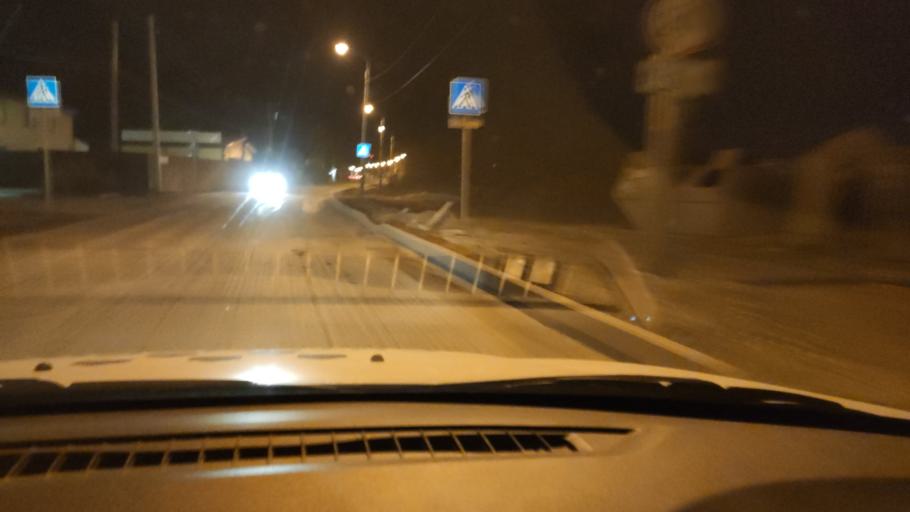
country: RU
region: Perm
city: Kondratovo
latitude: 57.9622
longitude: 56.1231
